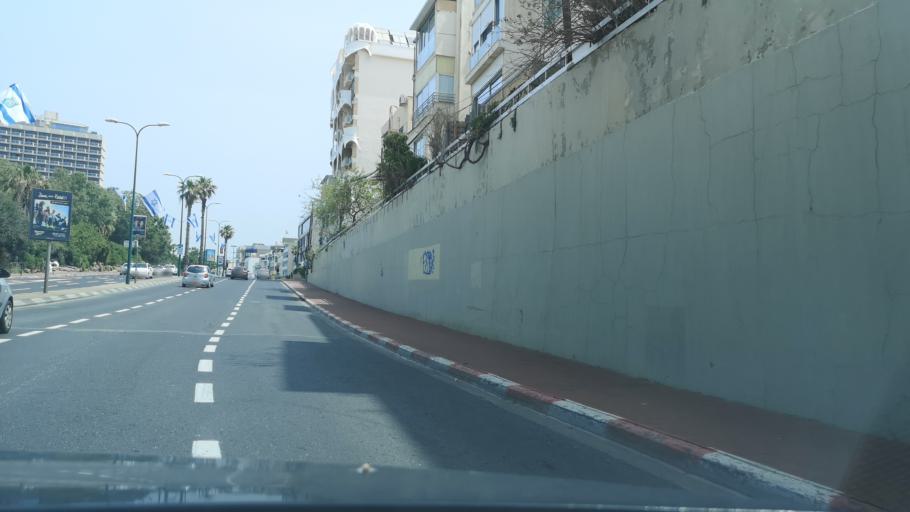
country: IL
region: Tel Aviv
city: Tel Aviv
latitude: 32.0864
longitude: 34.7700
